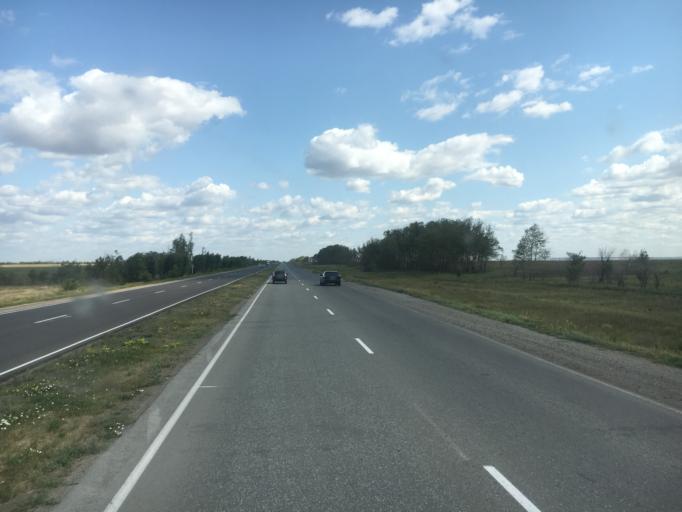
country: KZ
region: Qostanay
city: Kostanay
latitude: 53.0683
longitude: 63.4378
